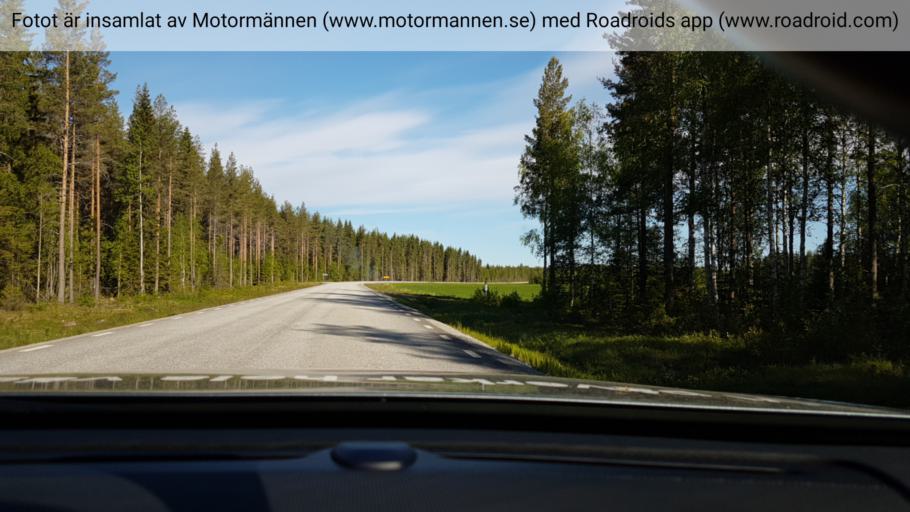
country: SE
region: Vaesterbotten
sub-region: Vindelns Kommun
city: Vindeln
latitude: 64.0906
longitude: 19.6148
